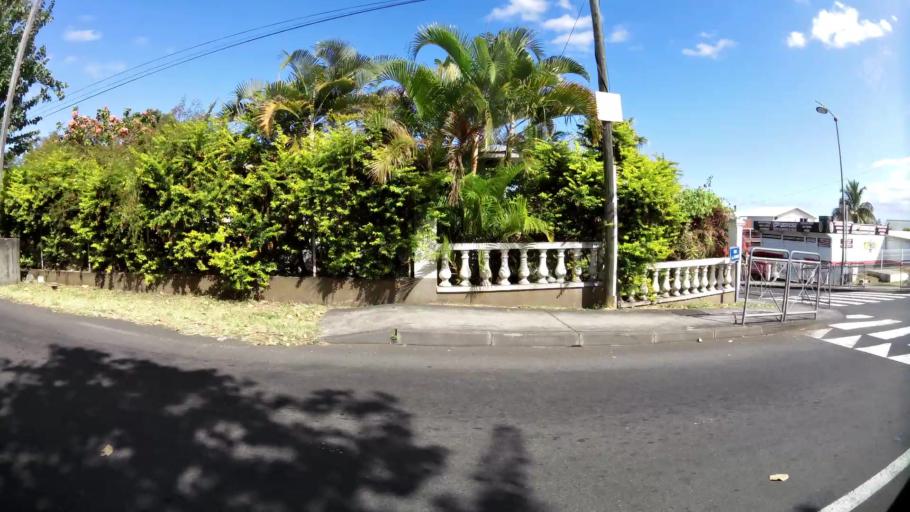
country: RE
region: Reunion
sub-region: Reunion
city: Le Tampon
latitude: -21.2821
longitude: 55.5103
